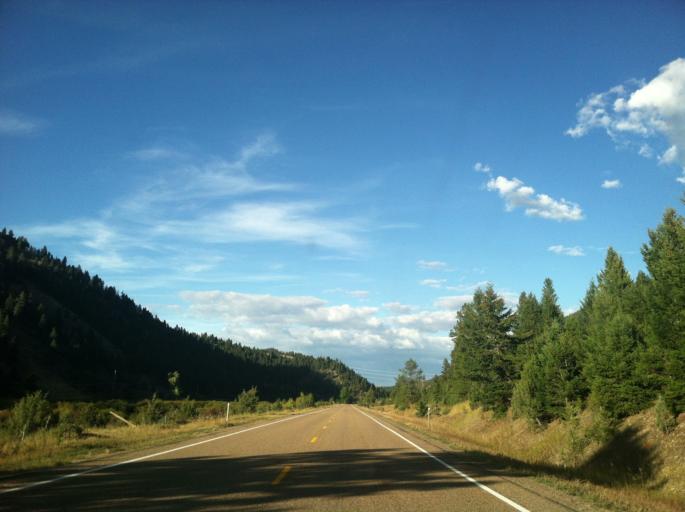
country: US
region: Montana
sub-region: Granite County
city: Philipsburg
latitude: 46.4333
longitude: -113.2691
